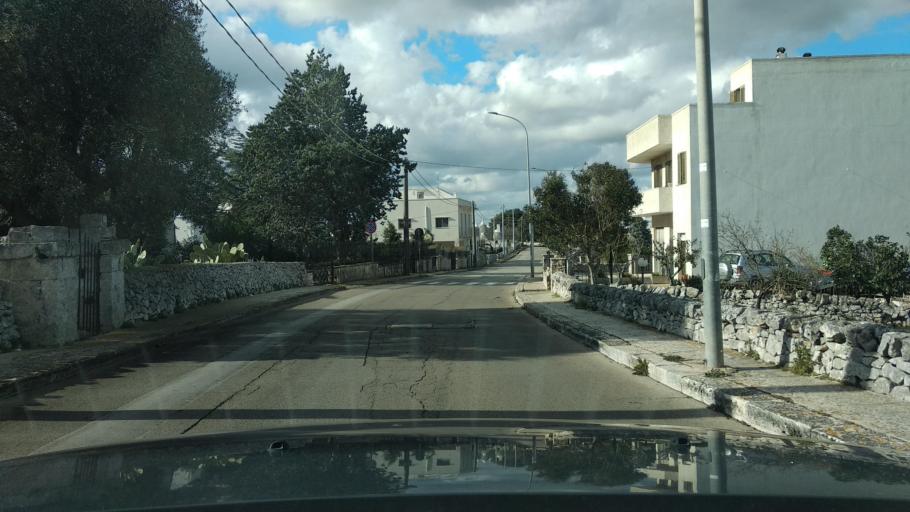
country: IT
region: Apulia
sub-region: Provincia di Brindisi
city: Cisternino
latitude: 40.7449
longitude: 17.4185
